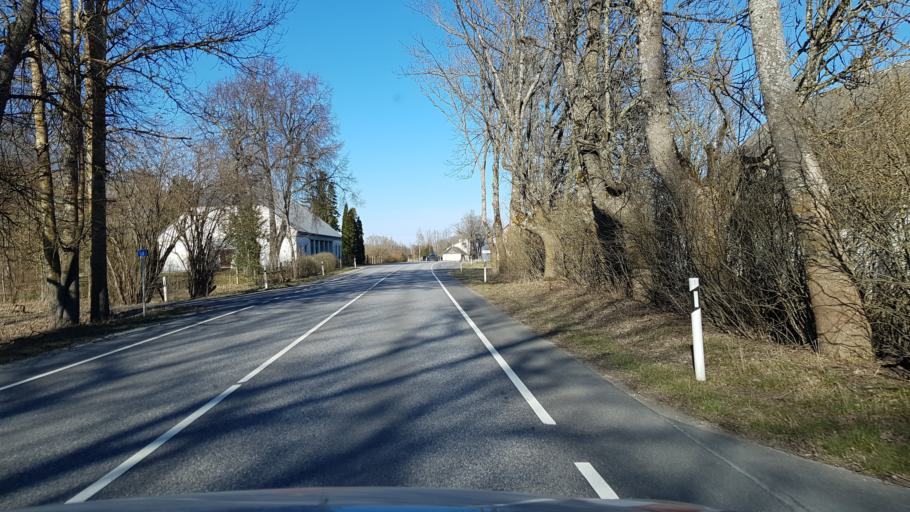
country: EE
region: Jogevamaa
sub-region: Mustvee linn
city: Mustvee
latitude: 58.9031
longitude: 26.9911
